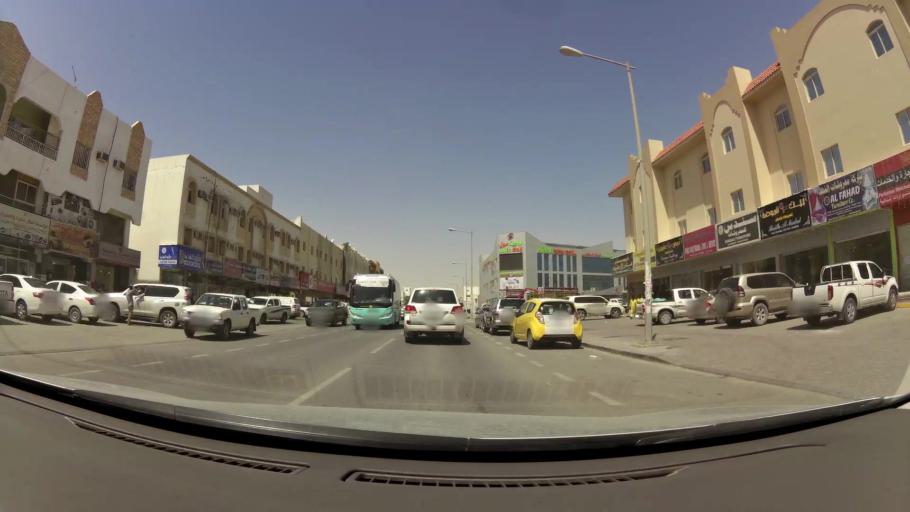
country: QA
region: Baladiyat ar Rayyan
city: Ar Rayyan
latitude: 25.2781
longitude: 51.4078
